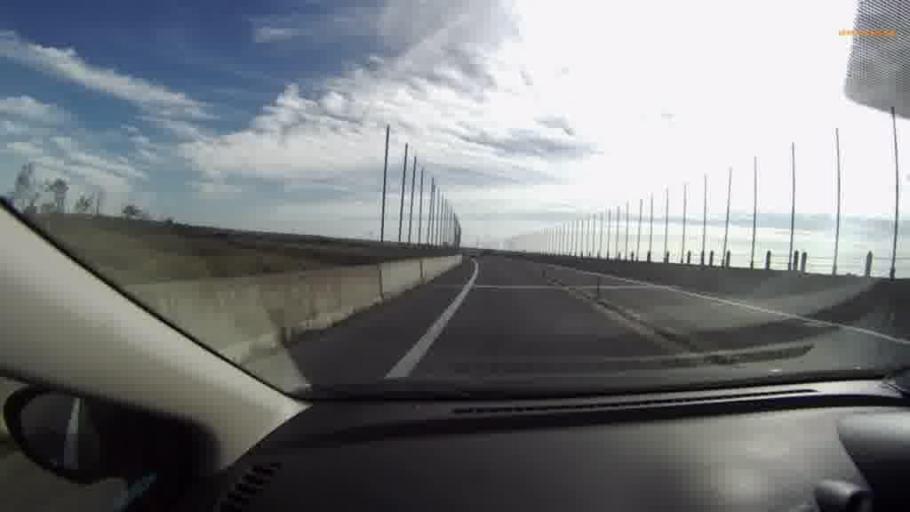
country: JP
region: Hokkaido
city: Kushiro
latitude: 43.0351
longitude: 144.3656
